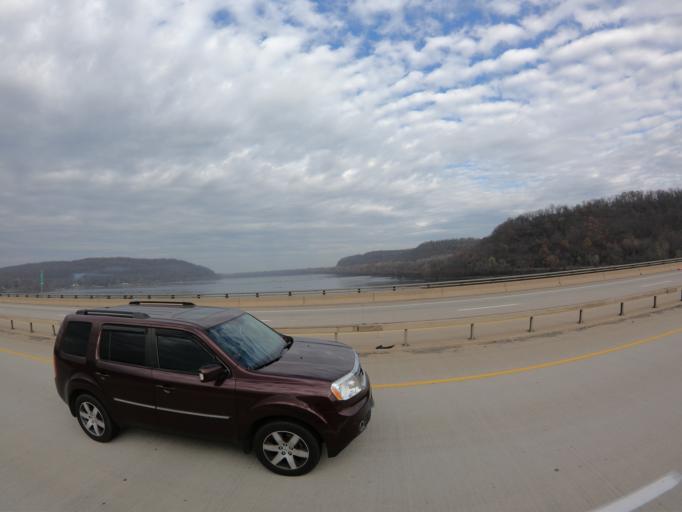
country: US
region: Pennsylvania
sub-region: Lancaster County
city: Columbia
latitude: 40.0364
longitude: -76.5182
